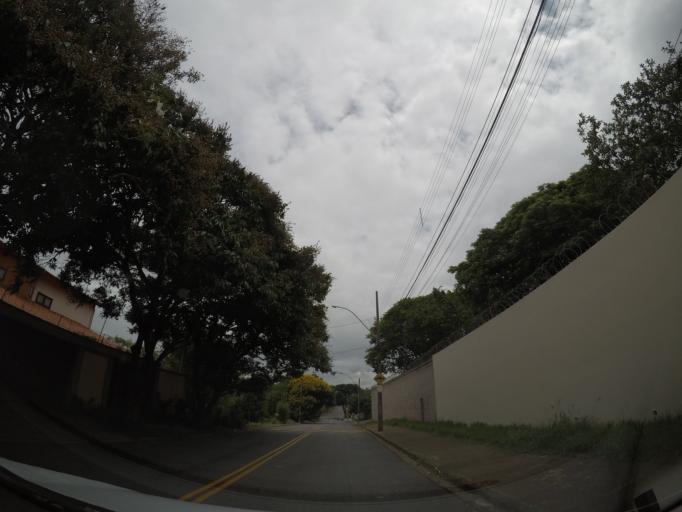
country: BR
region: Sao Paulo
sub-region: Campinas
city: Campinas
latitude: -22.9005
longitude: -47.0365
